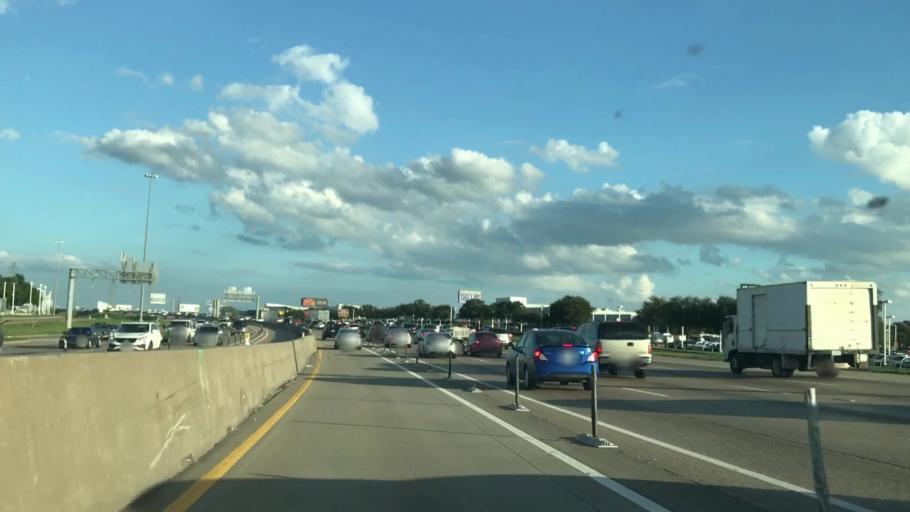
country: US
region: Texas
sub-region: Dallas County
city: Garland
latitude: 32.8733
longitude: -96.6813
